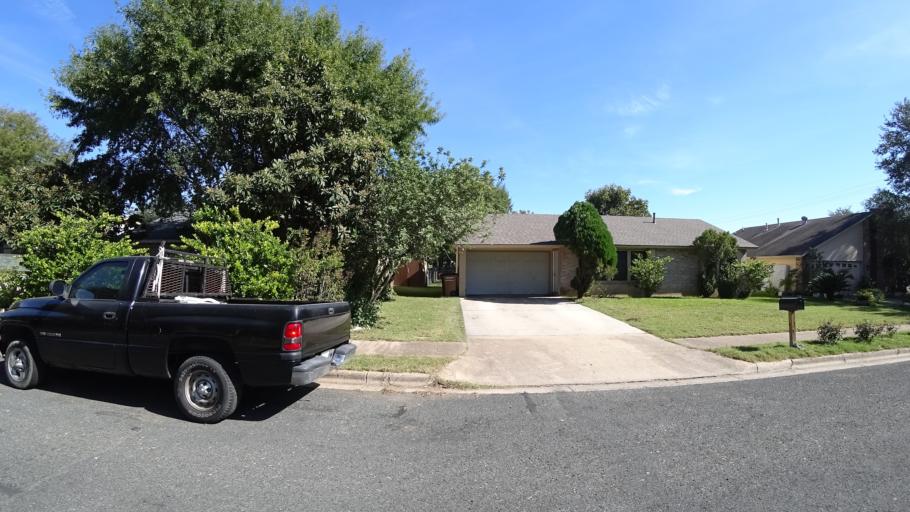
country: US
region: Texas
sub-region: Travis County
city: Austin
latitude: 30.1982
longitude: -97.7455
